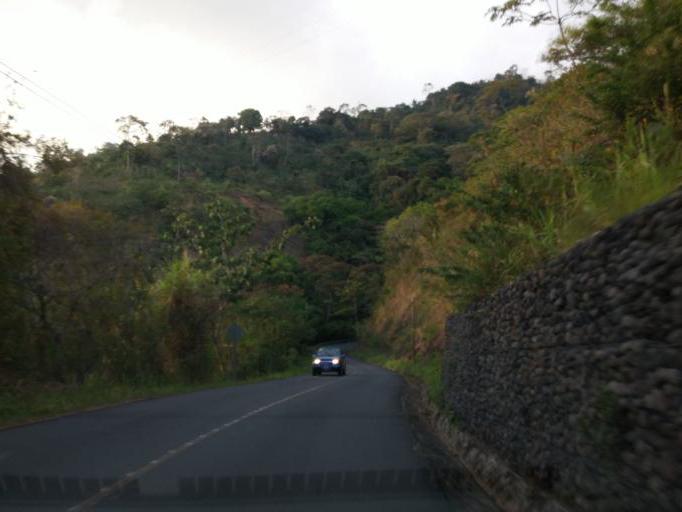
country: CR
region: San Jose
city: Palmichal
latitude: 9.8287
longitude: -84.1996
